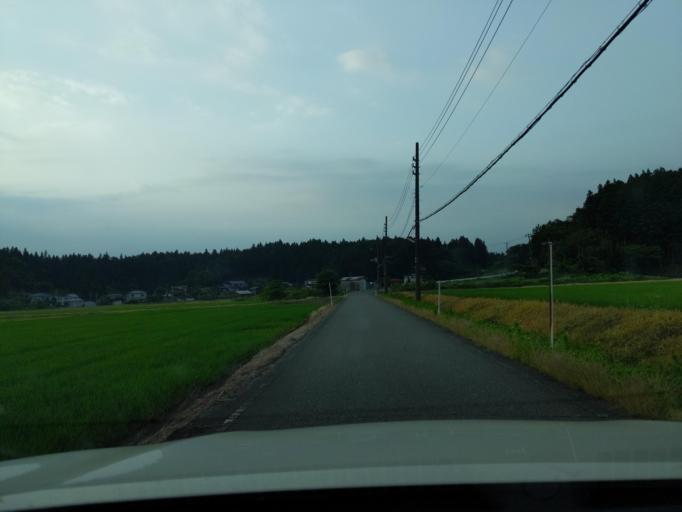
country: JP
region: Niigata
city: Kashiwazaki
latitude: 37.4380
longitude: 138.6518
